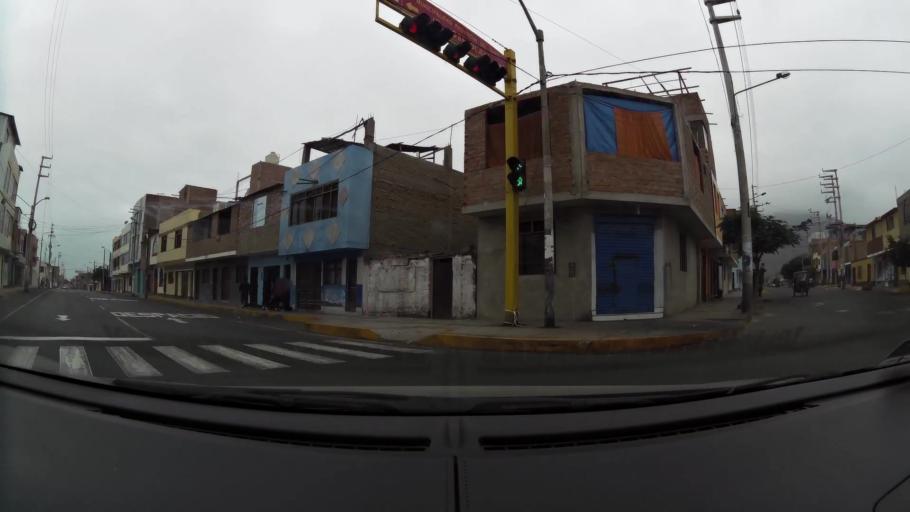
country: PE
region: Ancash
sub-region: Provincia de Santa
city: Chimbote
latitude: -9.0700
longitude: -78.5961
